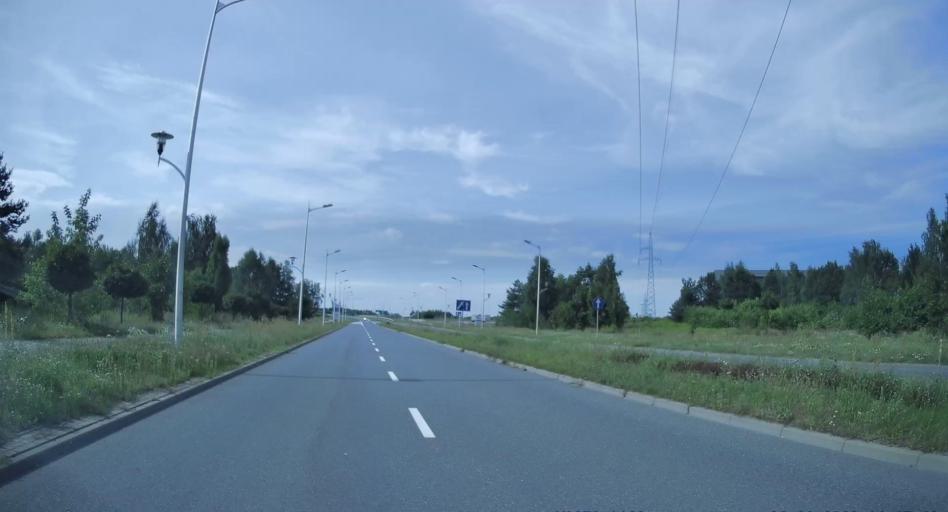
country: PL
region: Lodz Voivodeship
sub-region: Powiat tomaszowski
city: Tomaszow Mazowiecki
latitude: 51.5456
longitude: 19.9929
